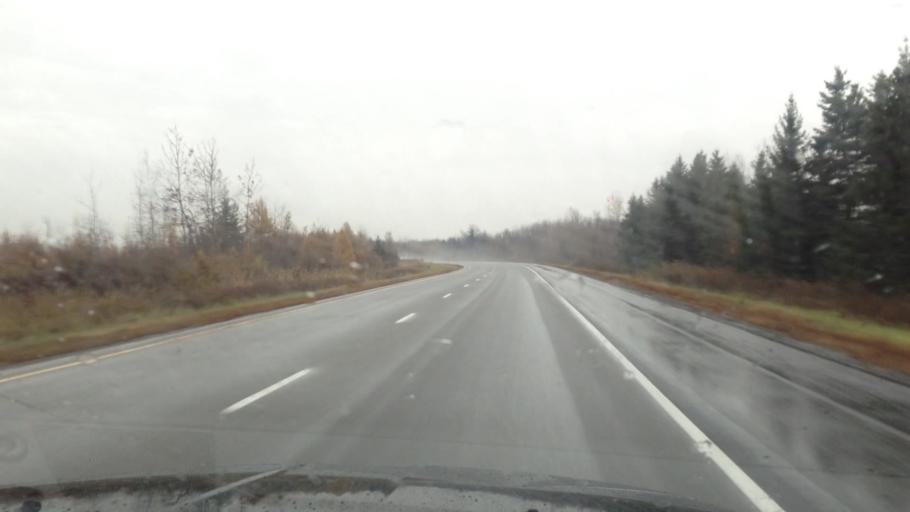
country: CA
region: Ontario
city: Casselman
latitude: 45.3077
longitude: -75.1488
